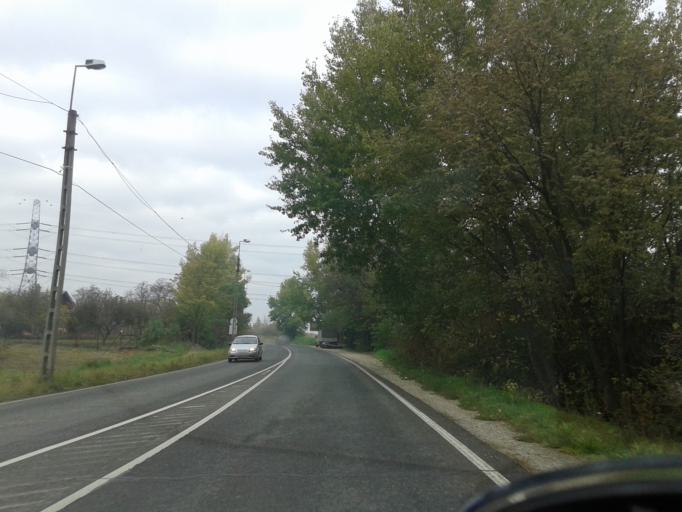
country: HU
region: Fejer
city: Ercsi
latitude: 47.2619
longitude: 18.8938
